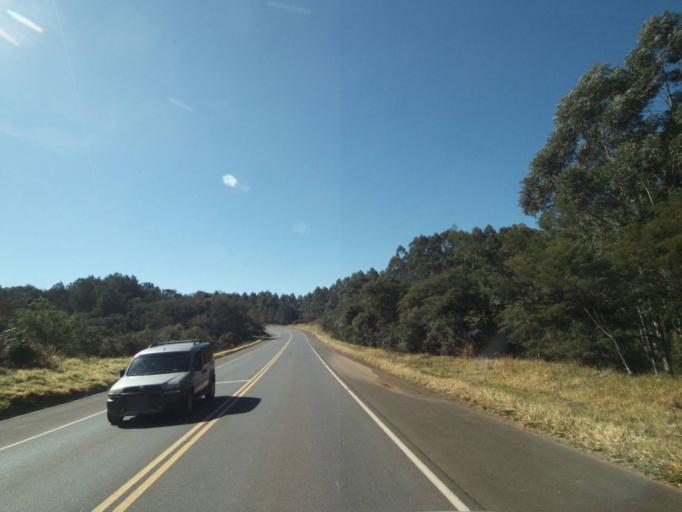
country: BR
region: Parana
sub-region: Tibagi
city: Tibagi
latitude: -24.5196
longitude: -50.4372
